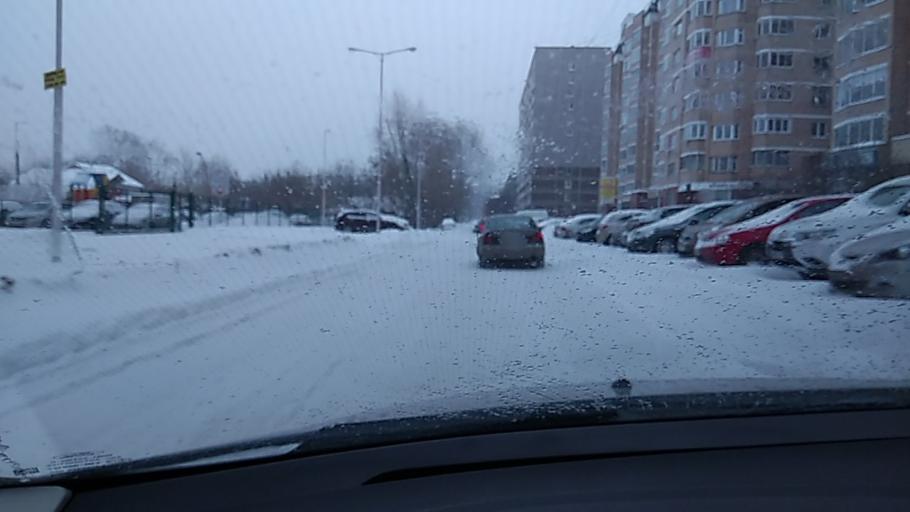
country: RU
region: Sverdlovsk
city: Sovkhoznyy
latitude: 56.8206
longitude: 60.5451
